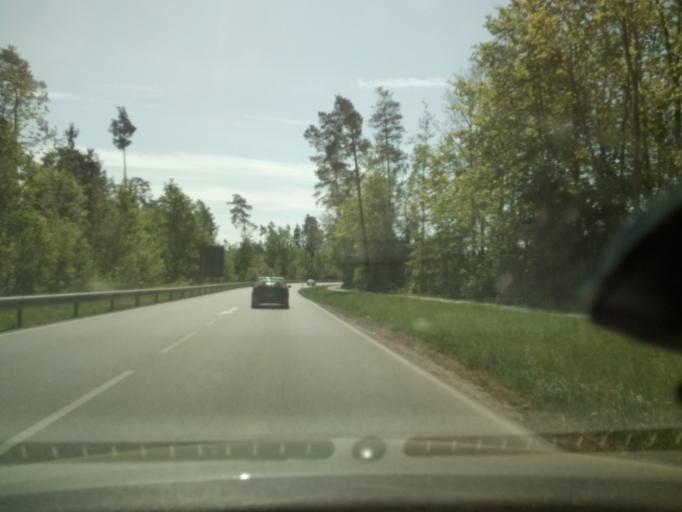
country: DE
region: Bavaria
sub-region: Upper Bavaria
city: Waldkraiburg
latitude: 48.2182
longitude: 12.4175
